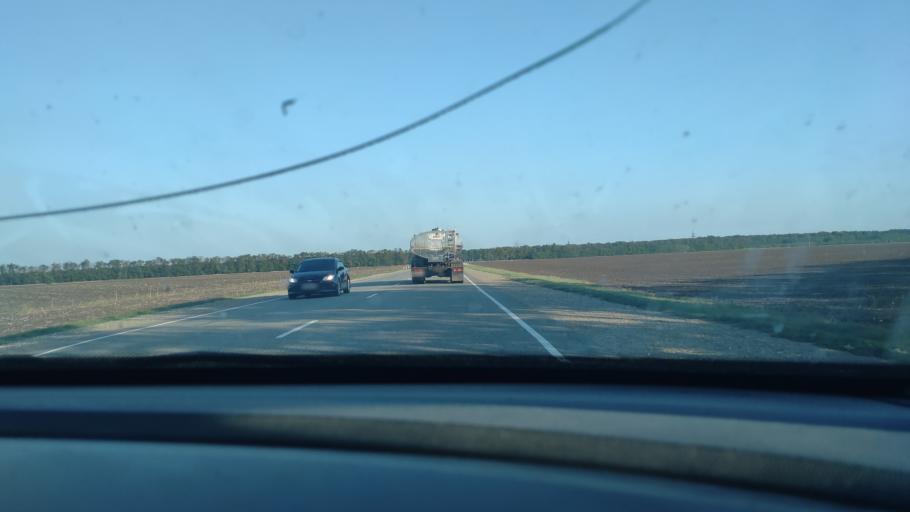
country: RU
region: Krasnodarskiy
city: Starominskaya
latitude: 46.4987
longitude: 39.0474
